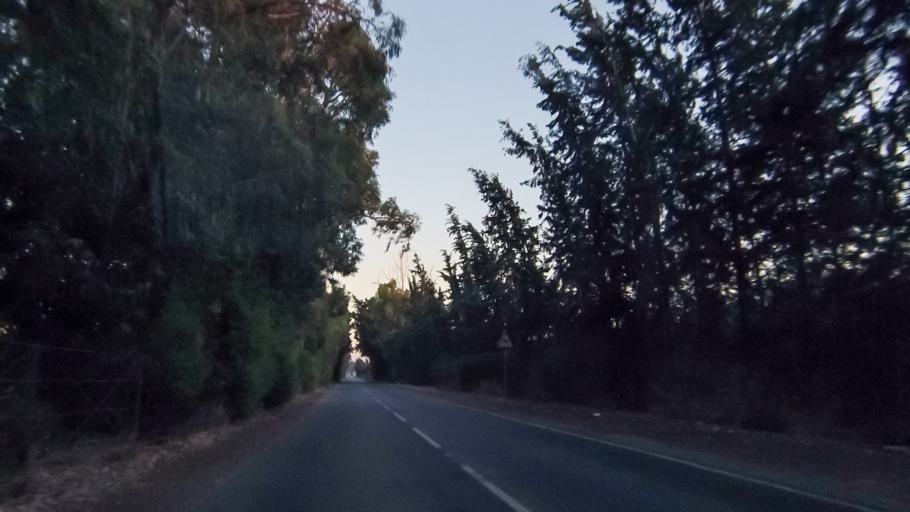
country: CY
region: Larnaka
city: Kolossi
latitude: 34.6497
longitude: 32.9425
